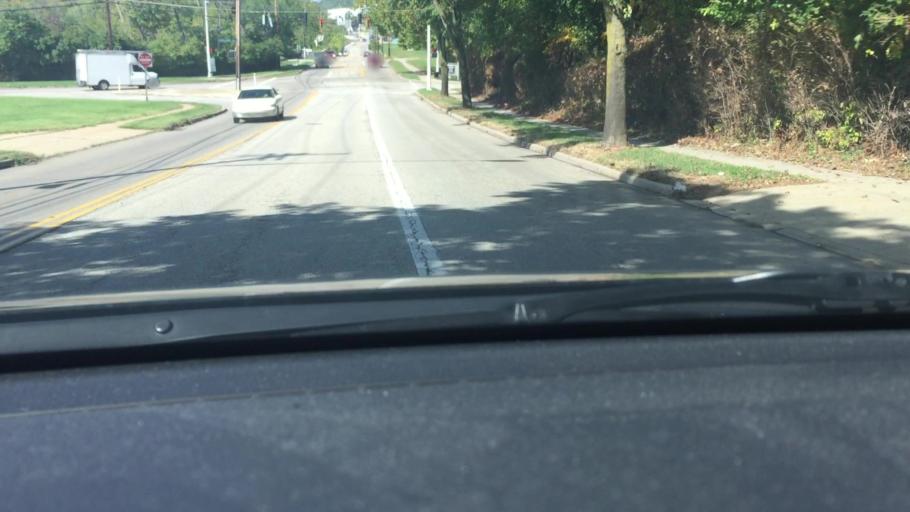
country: US
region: Ohio
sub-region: Hamilton County
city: Fairfax
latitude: 39.1652
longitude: -84.4142
